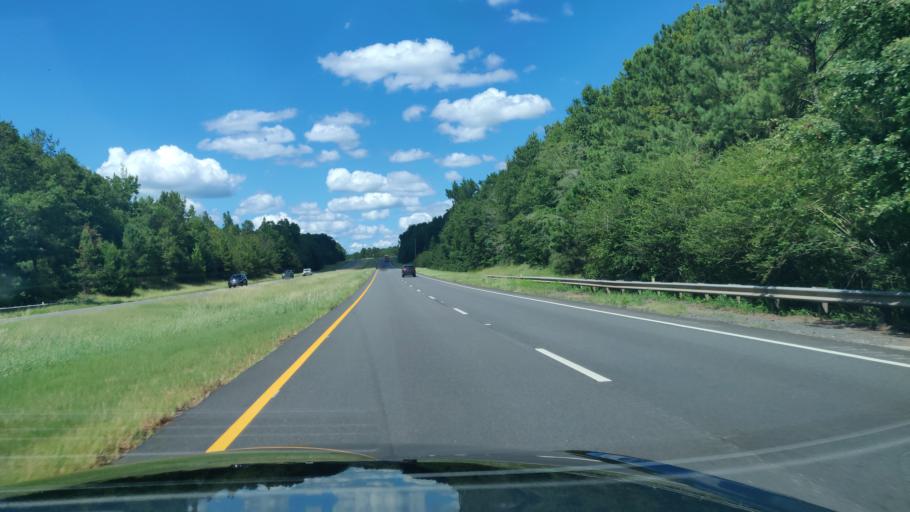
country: US
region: Georgia
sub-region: Stewart County
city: Richland
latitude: 32.0936
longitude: -84.6754
